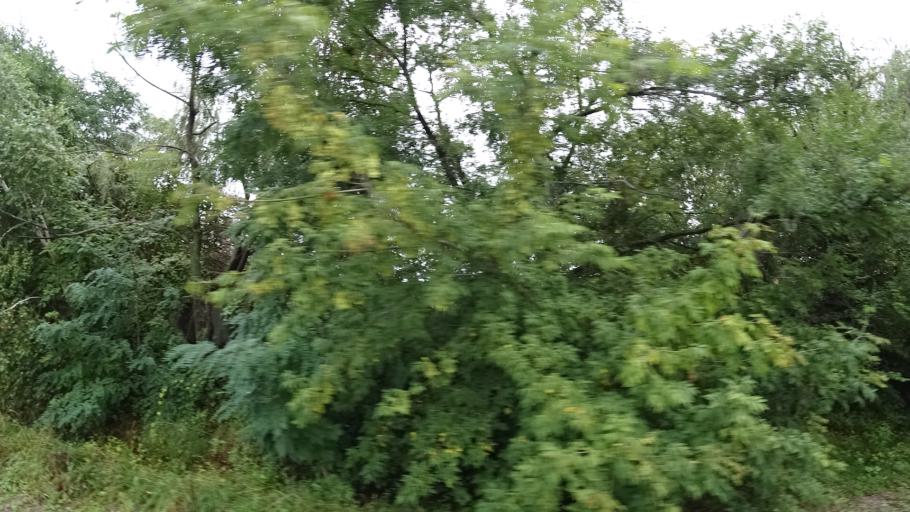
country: RU
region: Primorskiy
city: Monastyrishche
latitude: 44.1991
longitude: 132.4892
